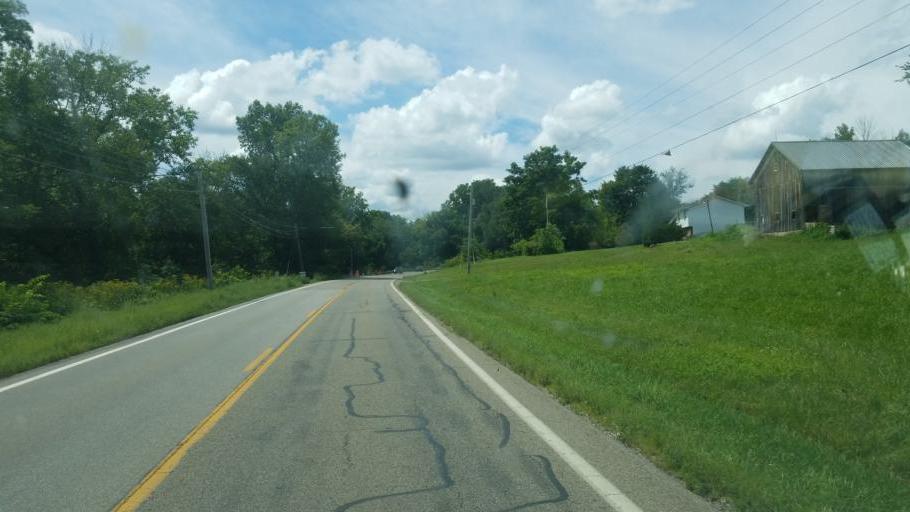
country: US
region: Ohio
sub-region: Knox County
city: Mount Vernon
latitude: 40.3474
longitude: -82.5752
